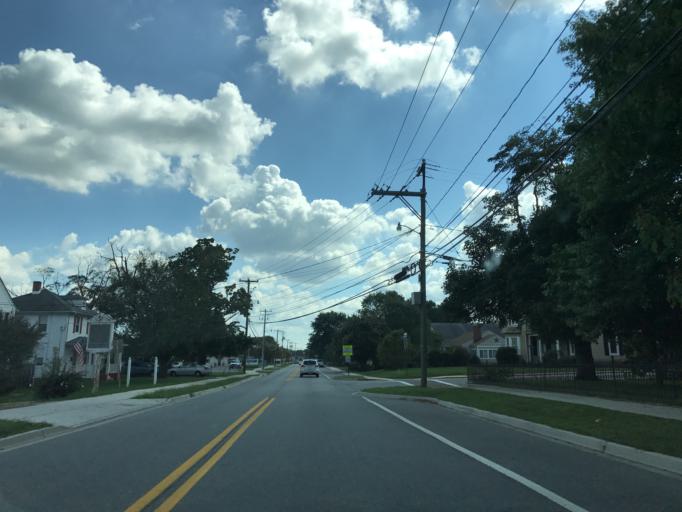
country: US
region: Maryland
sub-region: Queen Anne's County
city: Centreville
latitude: 39.0428
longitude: -76.0624
